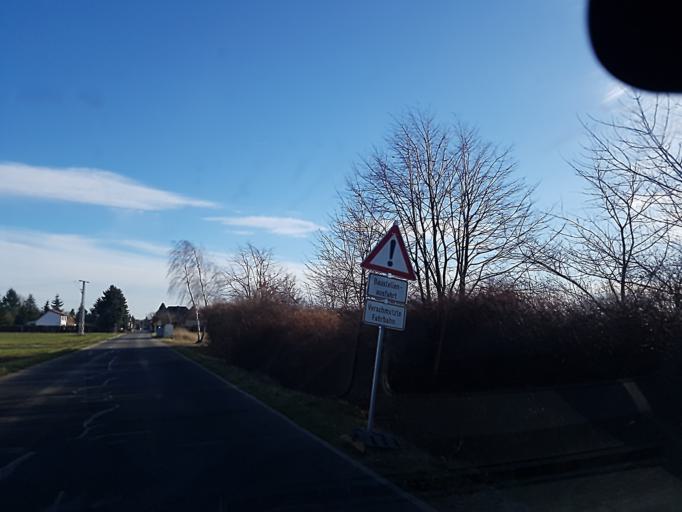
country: DE
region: Brandenburg
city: Finsterwalde
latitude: 51.6470
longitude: 13.7198
